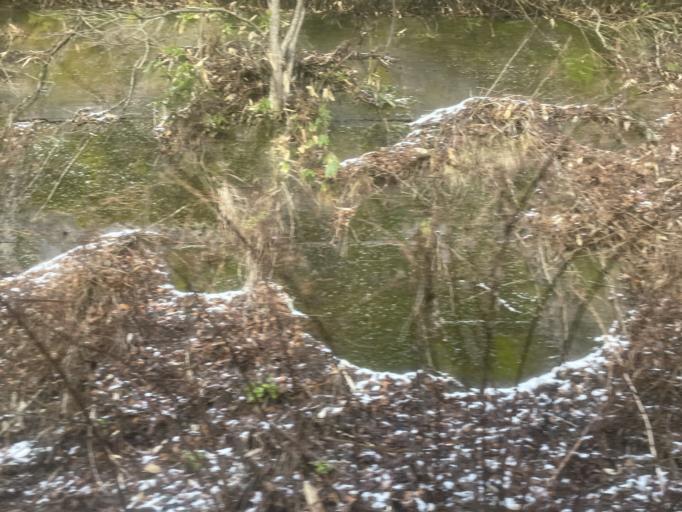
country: JP
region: Aomori
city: Goshogawara
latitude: 41.0783
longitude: 140.5316
